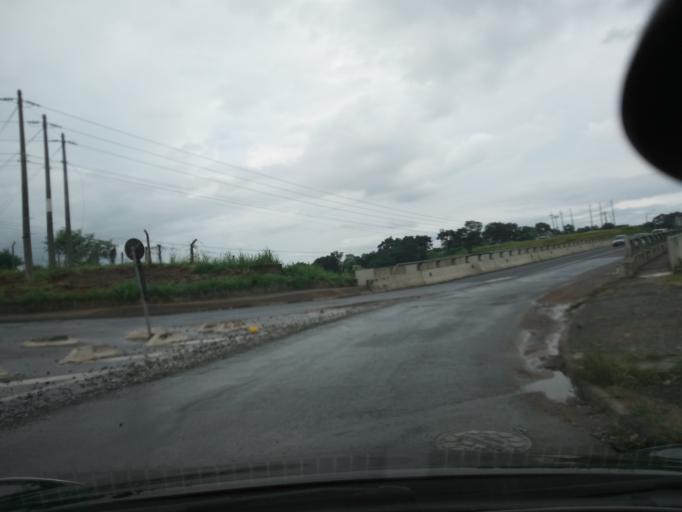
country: BR
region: Sao Paulo
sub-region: Campinas
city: Campinas
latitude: -22.9869
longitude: -47.1107
